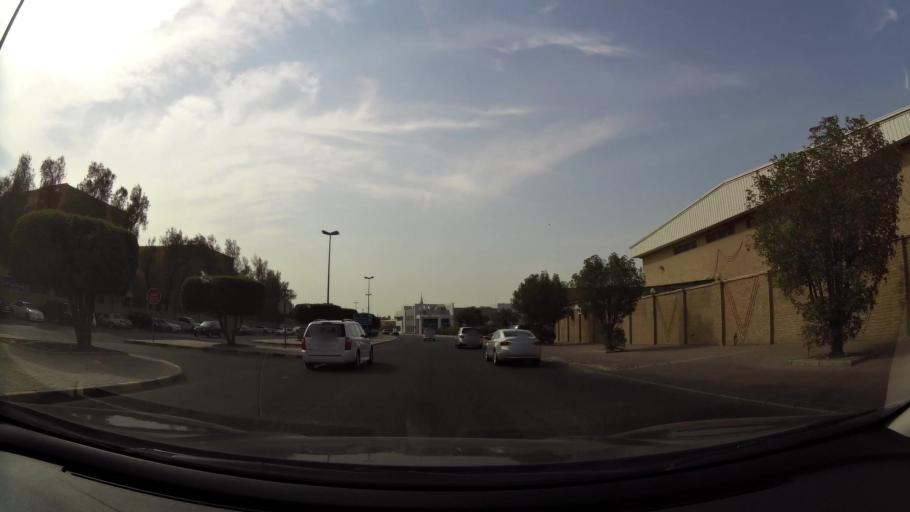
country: KW
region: Al Asimah
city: Ash Shamiyah
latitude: 29.3272
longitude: 47.9657
